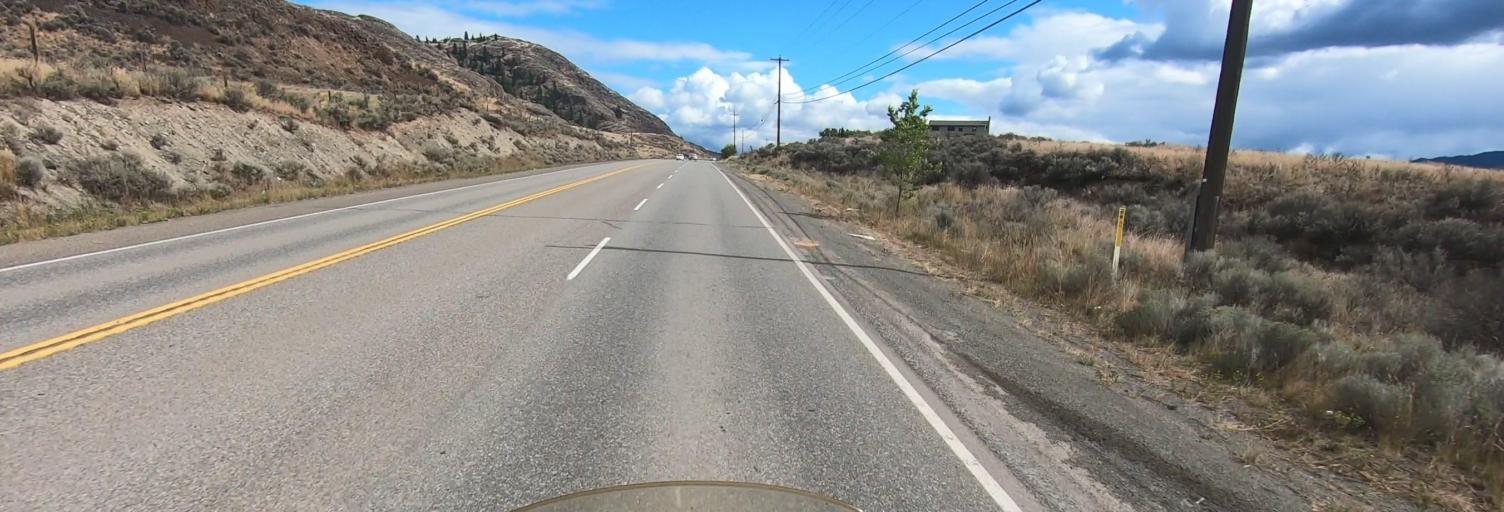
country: CA
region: British Columbia
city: Logan Lake
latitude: 50.7158
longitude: -120.6300
